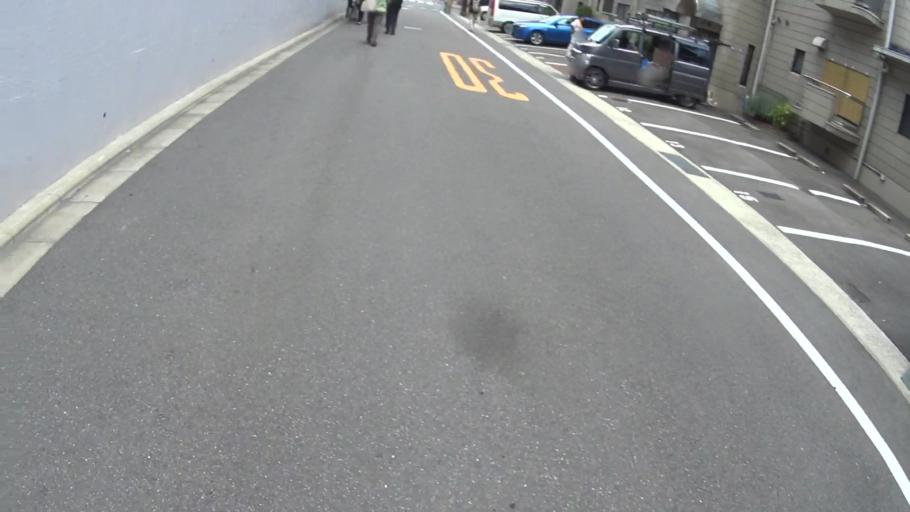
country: JP
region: Kyoto
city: Yawata
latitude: 34.9106
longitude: 135.6976
